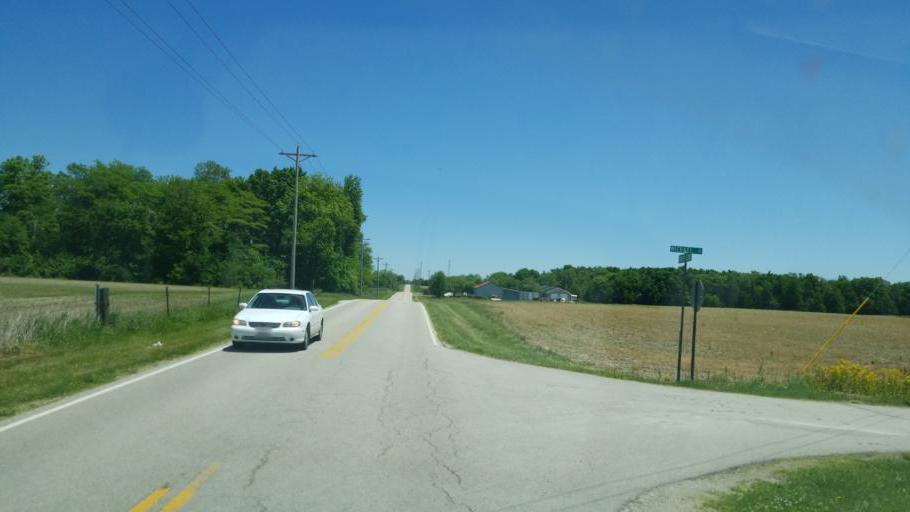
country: US
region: Ohio
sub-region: Darke County
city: Ansonia
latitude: 40.2648
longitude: -84.6527
